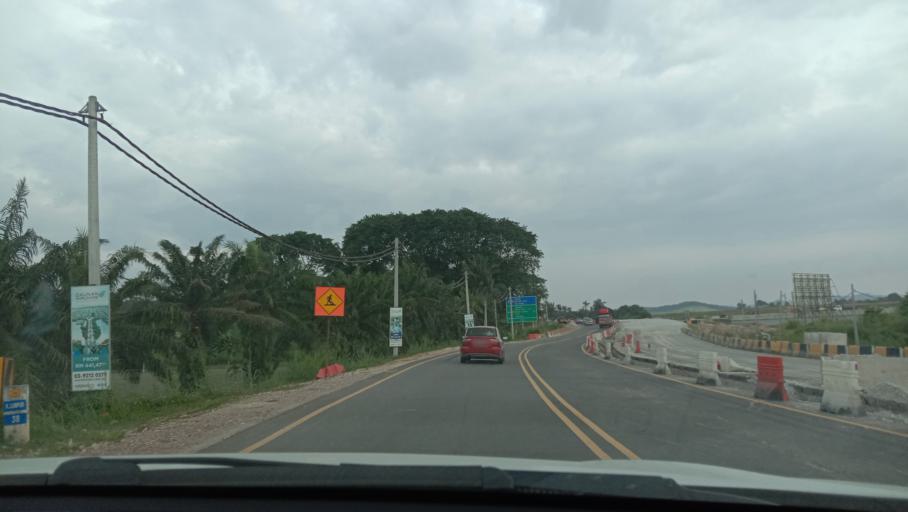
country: MY
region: Selangor
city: Batu Arang
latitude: 3.2653
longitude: 101.4573
